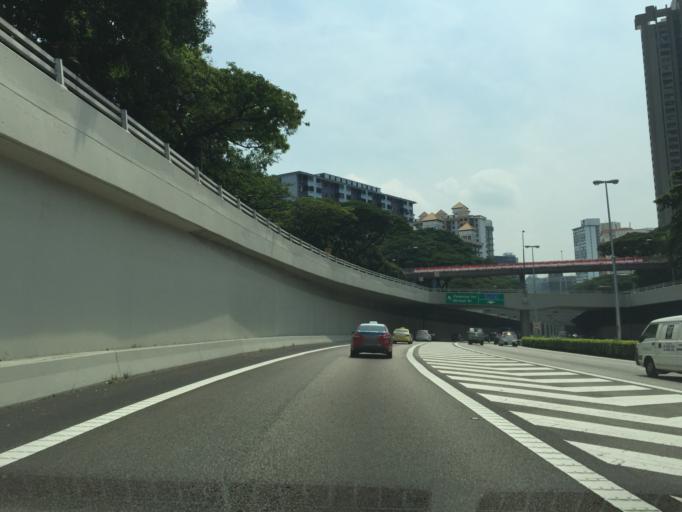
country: SG
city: Singapore
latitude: 1.2852
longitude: 103.8373
